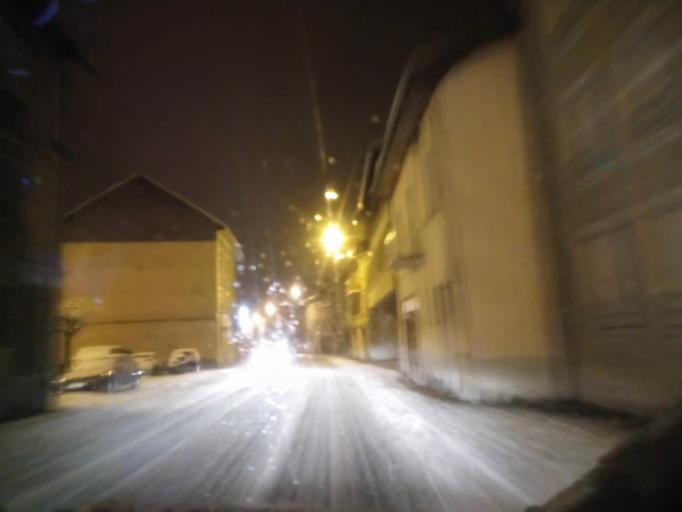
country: FR
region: Rhone-Alpes
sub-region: Departement de la Savoie
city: Saint-Michel-de-Maurienne
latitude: 45.2142
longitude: 6.4767
